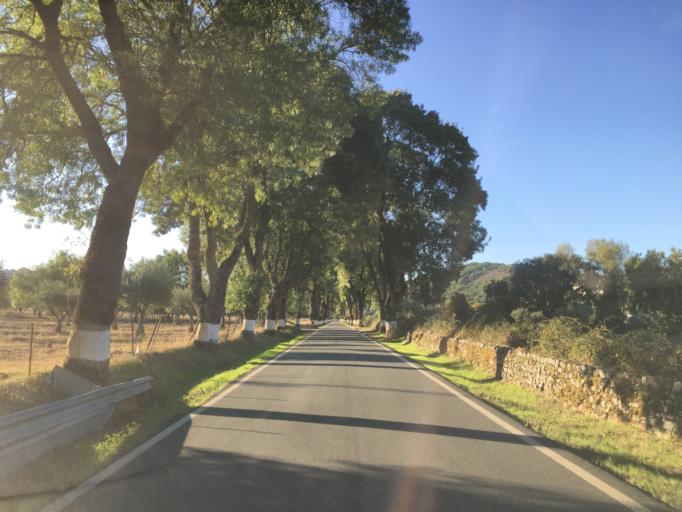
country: PT
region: Portalegre
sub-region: Marvao
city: Marvao
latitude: 39.3793
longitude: -7.3902
